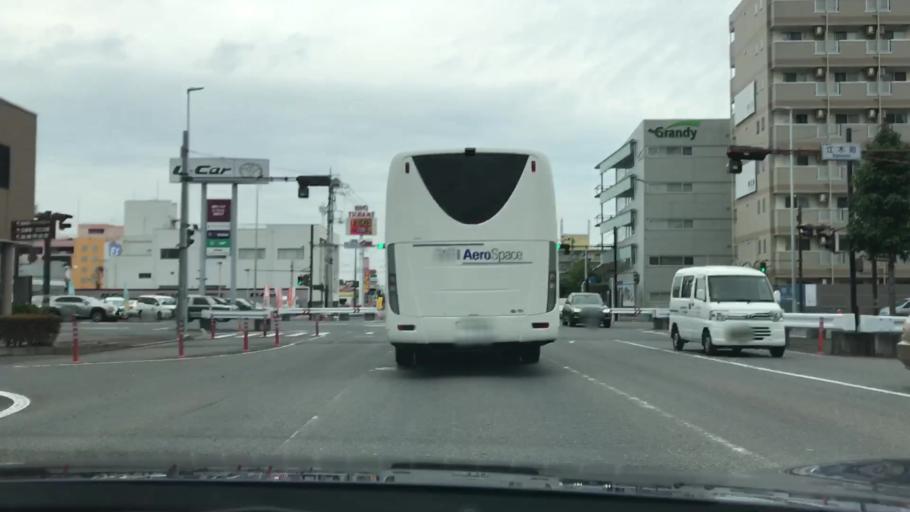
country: JP
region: Gunma
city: Takasaki
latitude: 36.3276
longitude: 139.0145
